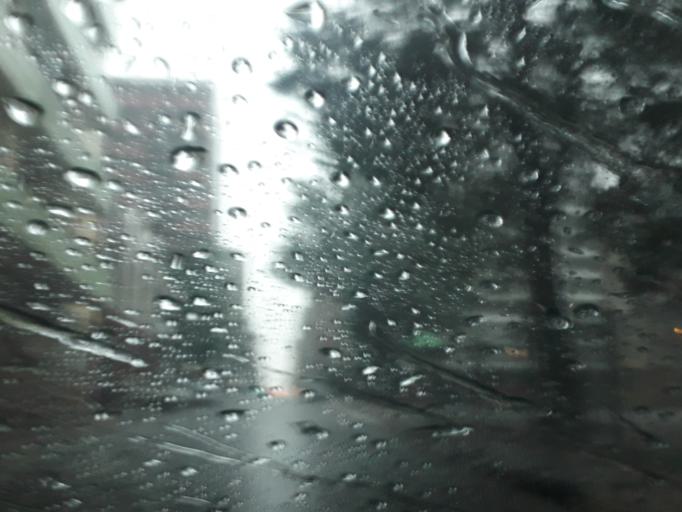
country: ZA
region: Gauteng
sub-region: City of Johannesburg Metropolitan Municipality
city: Johannesburg
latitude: -26.1868
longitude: 28.0460
